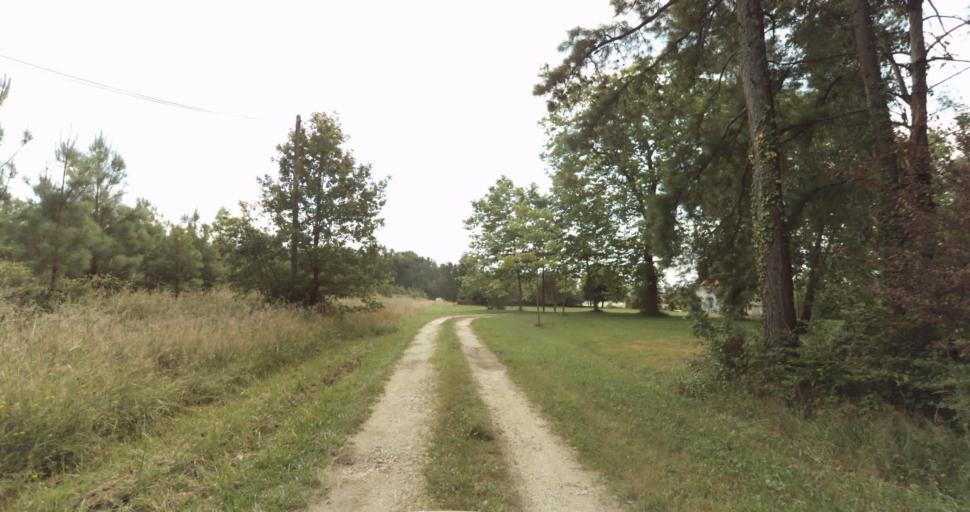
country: FR
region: Aquitaine
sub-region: Departement de la Gironde
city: Bazas
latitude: 44.4569
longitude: -0.1859
